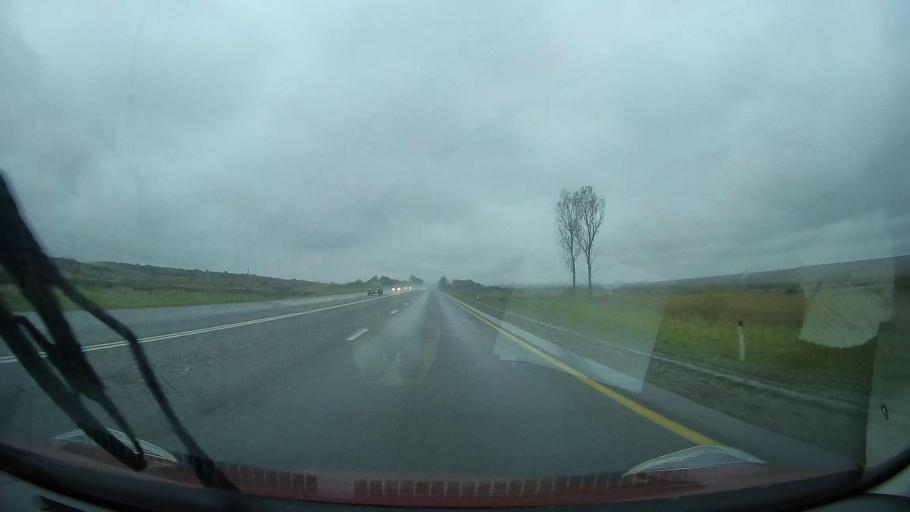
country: RU
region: Stavropol'skiy
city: Nevinnomyssk
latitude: 44.6287
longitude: 42.0396
